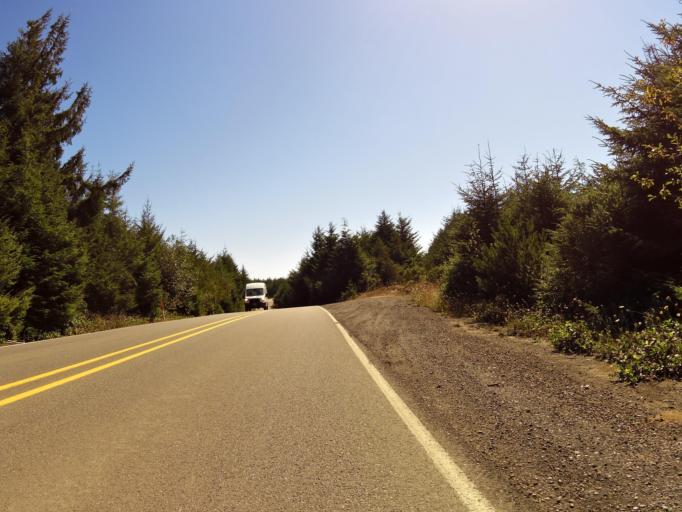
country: US
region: Oregon
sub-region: Coos County
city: Barview
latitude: 43.2736
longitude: -124.3554
